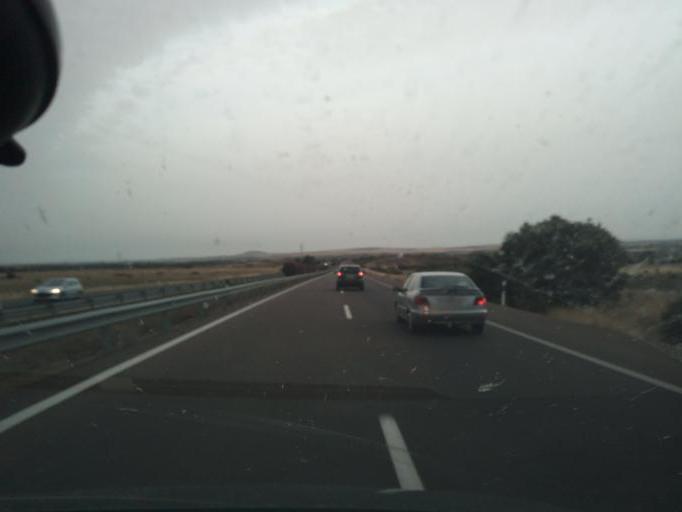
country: ES
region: Extremadura
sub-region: Provincia de Badajoz
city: San Pedro de Merida
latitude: 38.9494
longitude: -6.2123
